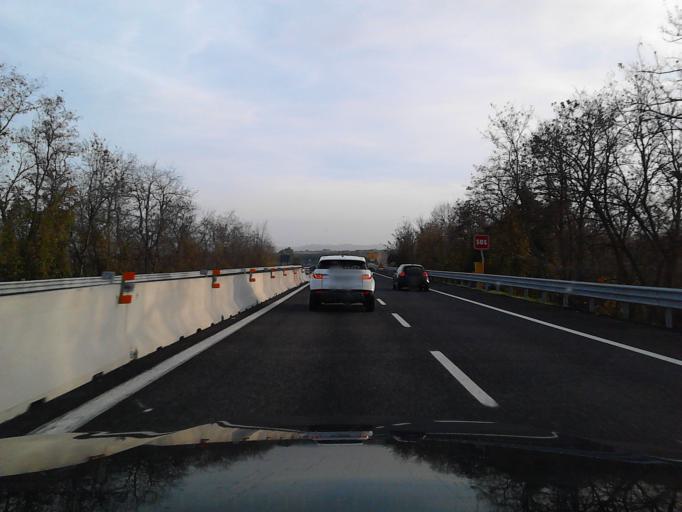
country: IT
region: Abruzzo
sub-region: Provincia di Chieti
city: Ortona
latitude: 42.3195
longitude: 14.3989
